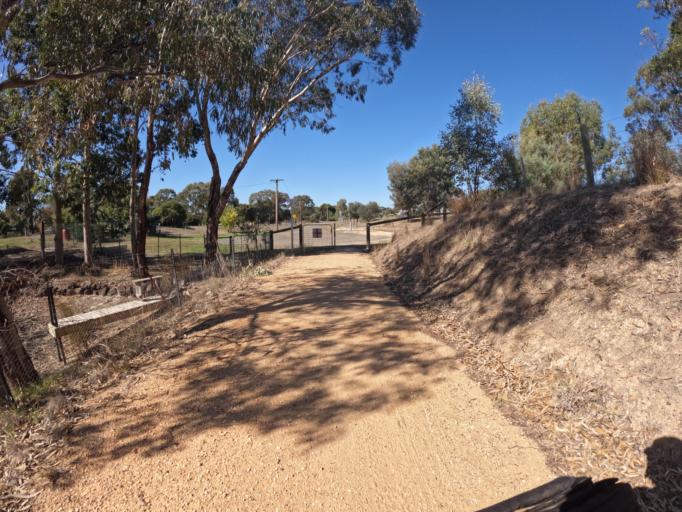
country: AU
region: Victoria
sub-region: Greater Bendigo
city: Kennington
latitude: -36.8254
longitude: 144.5838
